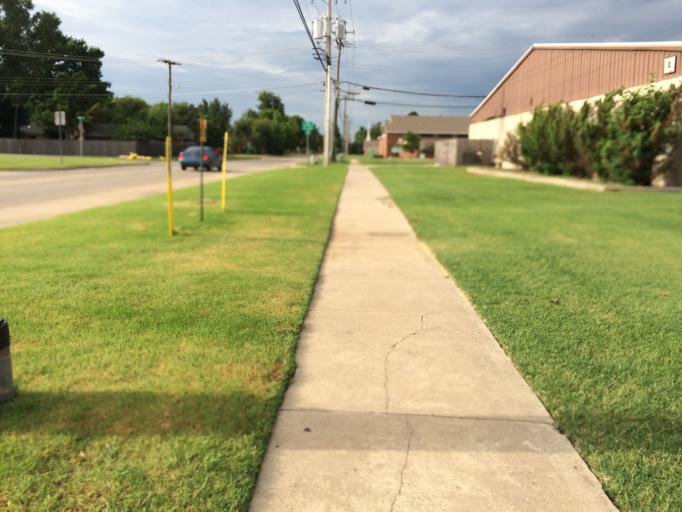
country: US
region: Oklahoma
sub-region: Cleveland County
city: Norman
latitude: 35.2262
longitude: -97.4591
